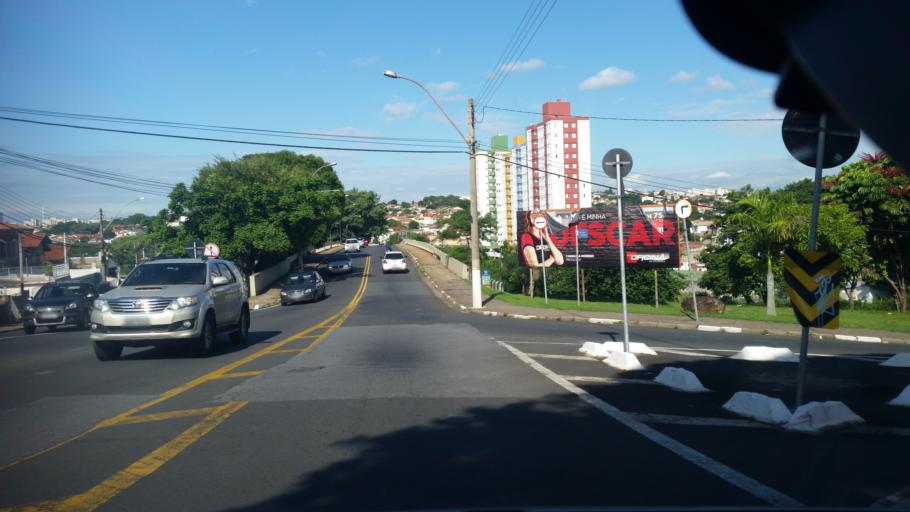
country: BR
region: Sao Paulo
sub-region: Campinas
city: Campinas
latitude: -22.8766
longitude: -47.0401
